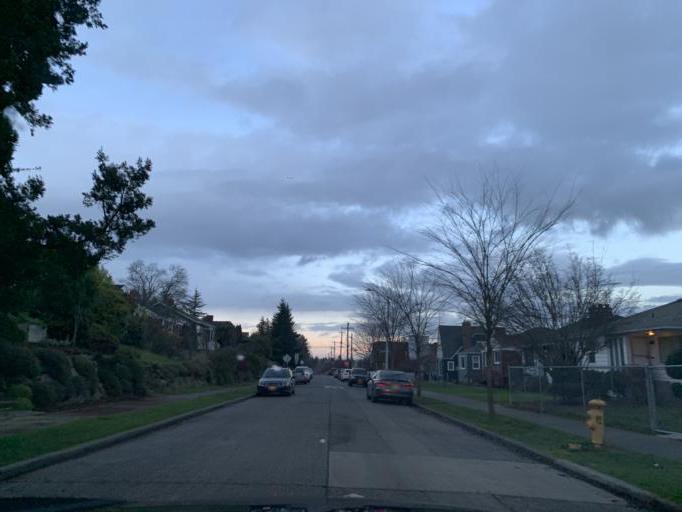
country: US
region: Washington
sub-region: King County
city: Seattle
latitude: 47.5662
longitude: -122.3147
